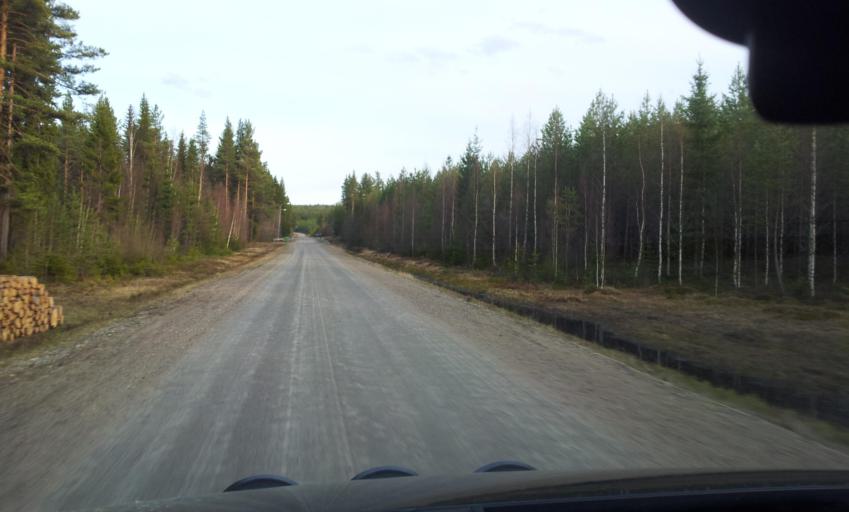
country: SE
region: Gaevleborg
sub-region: Ljusdals Kommun
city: Farila
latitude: 62.1206
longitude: 15.6796
